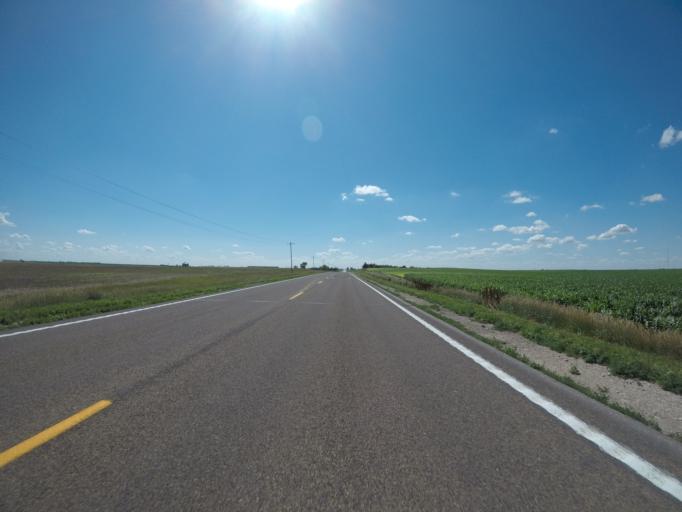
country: US
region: Nebraska
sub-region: Chase County
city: Imperial
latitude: 40.5375
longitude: -101.8307
